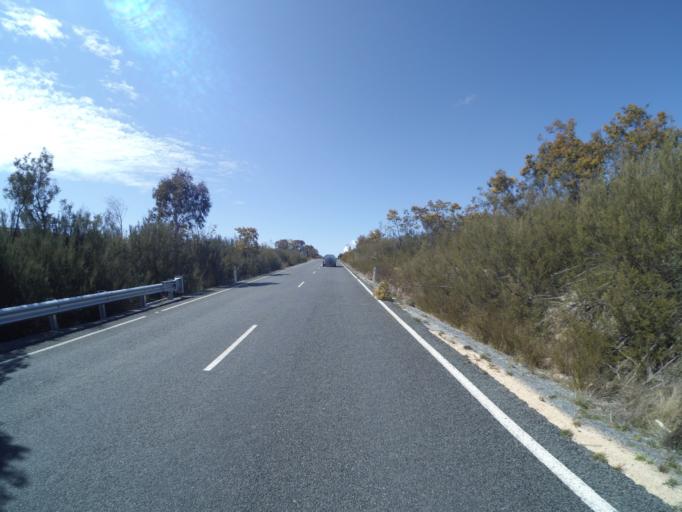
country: AU
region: Australian Capital Territory
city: Macarthur
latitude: -35.4570
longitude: 149.0125
